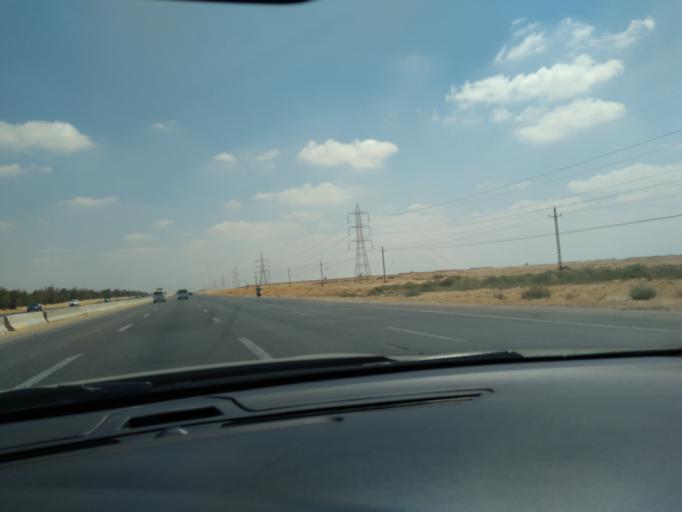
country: EG
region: Al Isma'iliyah
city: At Tall al Kabir
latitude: 30.3928
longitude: 31.9701
